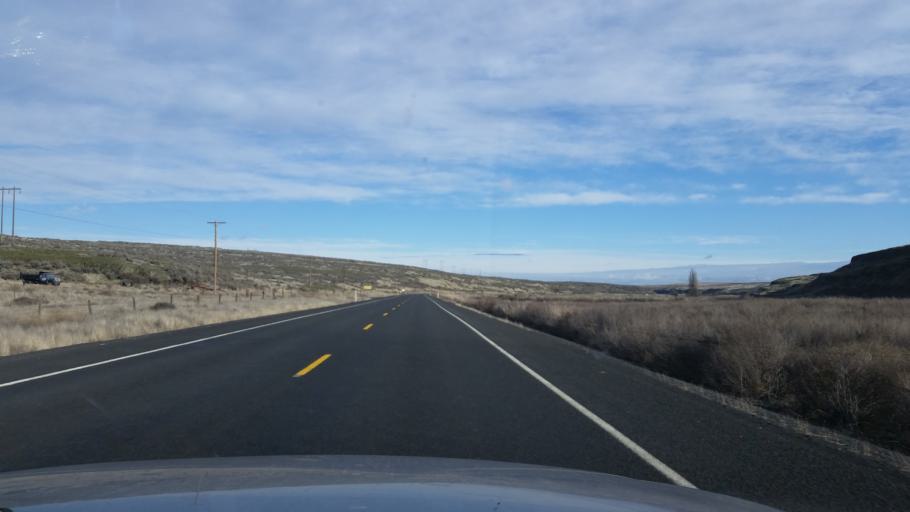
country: US
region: Washington
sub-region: Adams County
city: Ritzville
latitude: 47.3567
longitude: -118.5196
